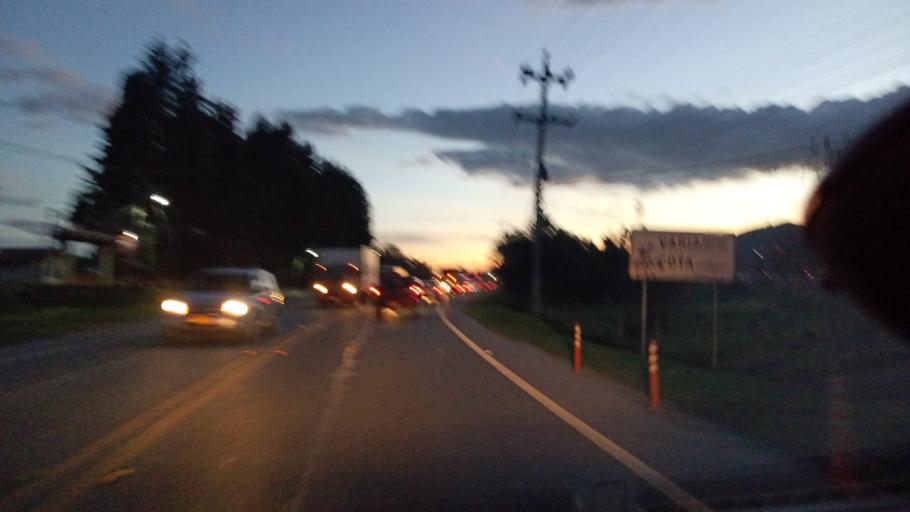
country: CO
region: Cundinamarca
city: Cota
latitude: 4.8286
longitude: -74.0903
